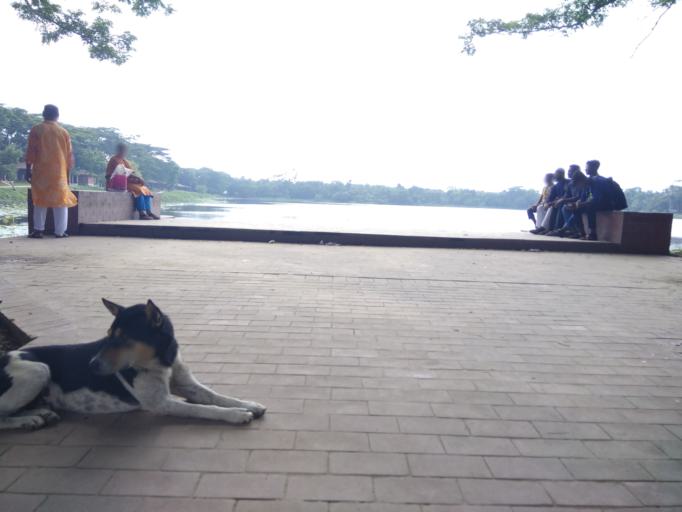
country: BD
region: Khulna
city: Khulna
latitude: 22.6747
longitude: 89.7415
